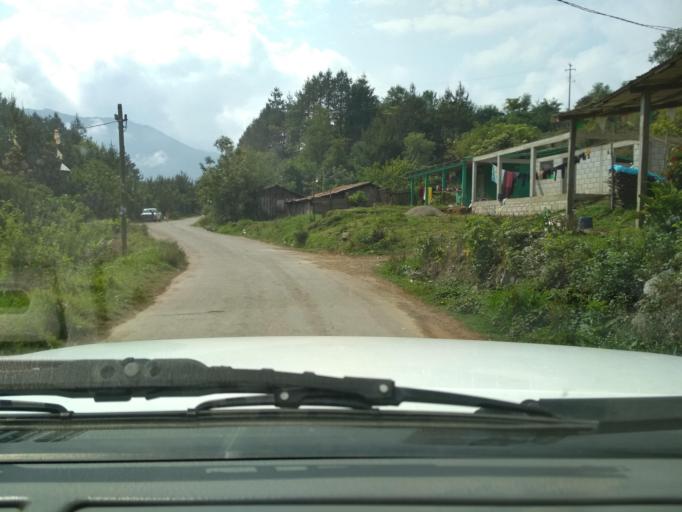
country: MX
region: Veracruz
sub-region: Camerino Z. Mendoza
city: Necoxtla
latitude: 18.7667
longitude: -97.1514
